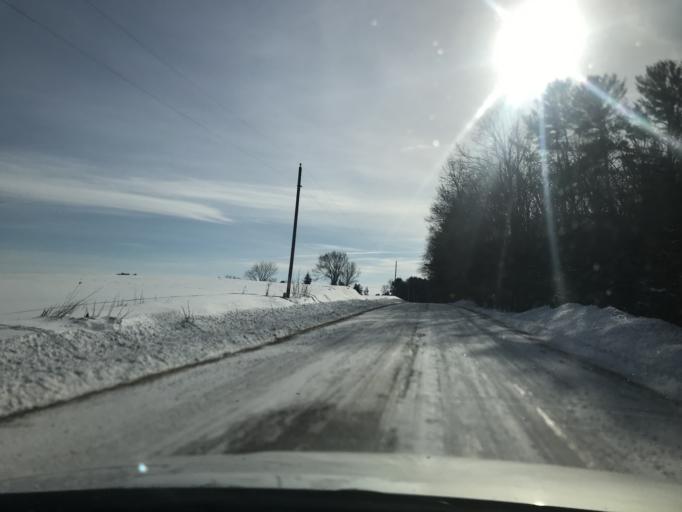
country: US
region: Wisconsin
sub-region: Oconto County
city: Gillett
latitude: 45.1169
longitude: -88.2401
